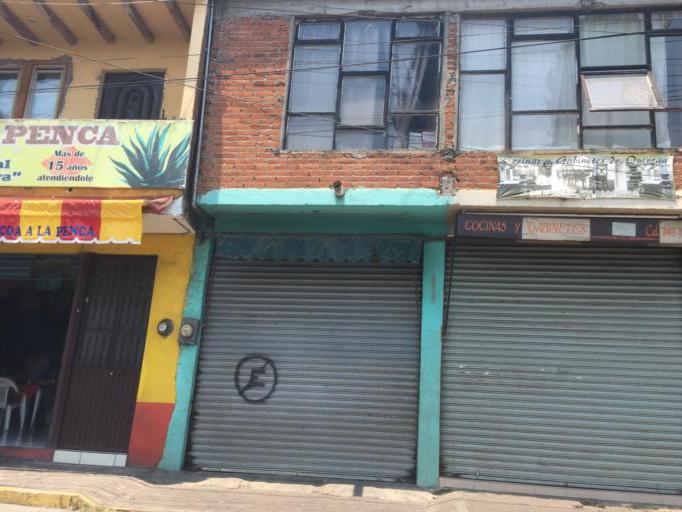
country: MX
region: Michoacan
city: Quiroga
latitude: 19.6636
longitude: -101.5272
